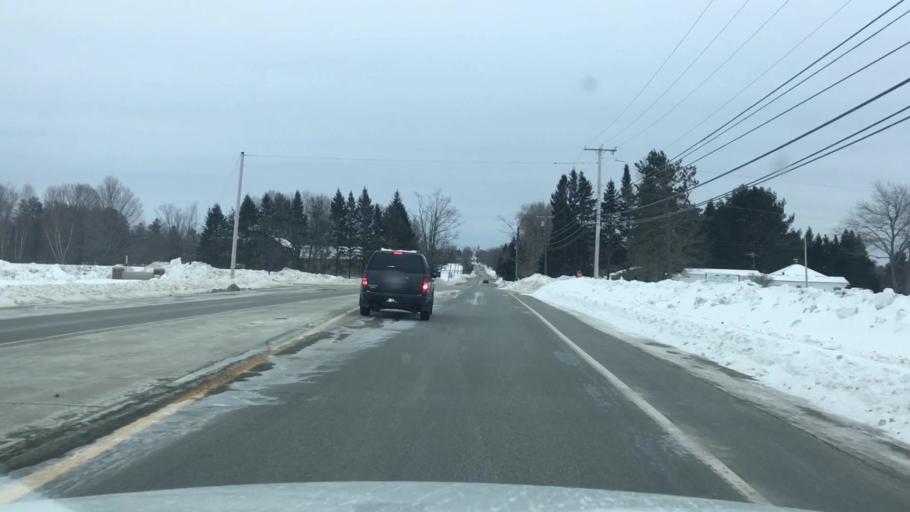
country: US
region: Maine
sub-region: Penobscot County
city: Charleston
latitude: 45.0171
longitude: -69.0280
